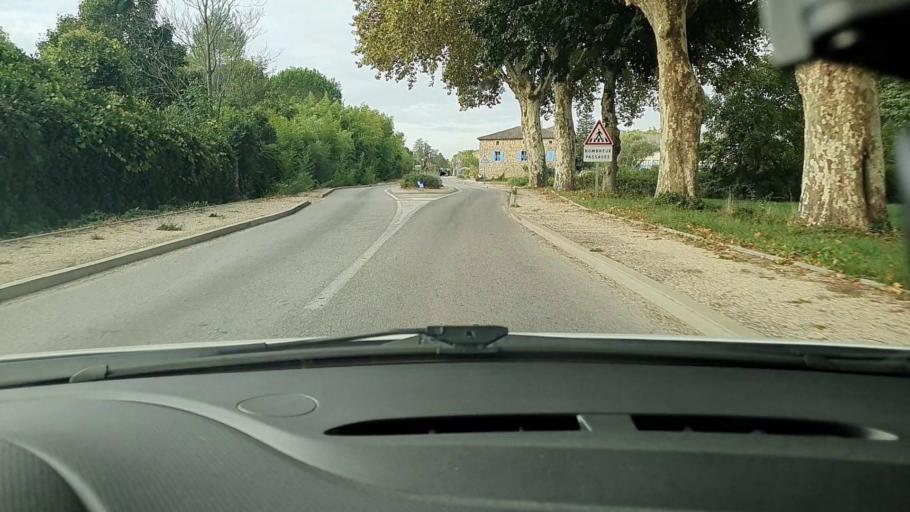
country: FR
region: Languedoc-Roussillon
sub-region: Departement du Gard
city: Saint-Ambroix
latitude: 44.2282
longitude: 4.2746
